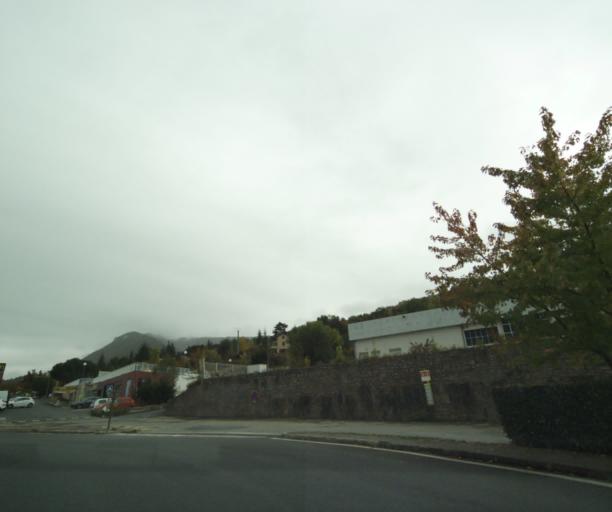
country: FR
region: Midi-Pyrenees
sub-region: Departement de l'Aveyron
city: Millau
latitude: 44.0910
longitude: 3.0810
